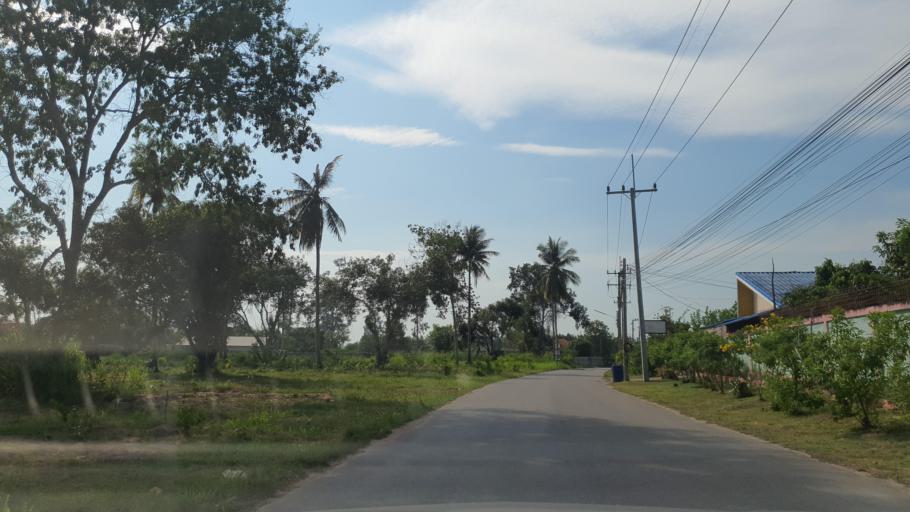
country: TH
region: Chon Buri
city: Sattahip
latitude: 12.7935
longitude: 100.9377
